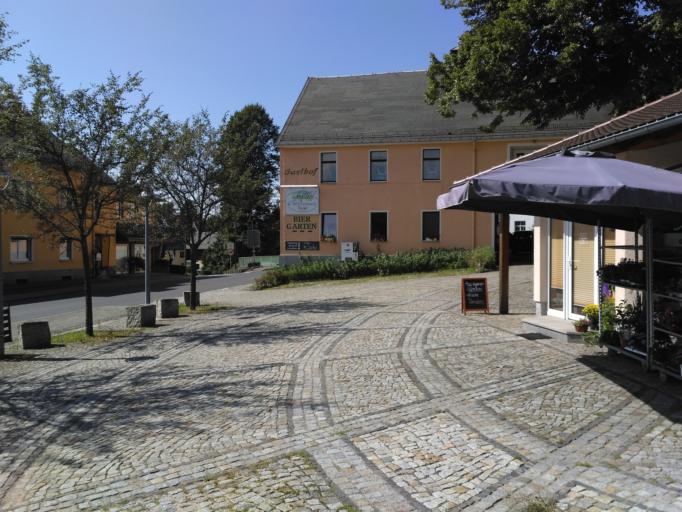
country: DE
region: Saxony
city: Oberlichtenau
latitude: 51.2453
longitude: 13.9799
